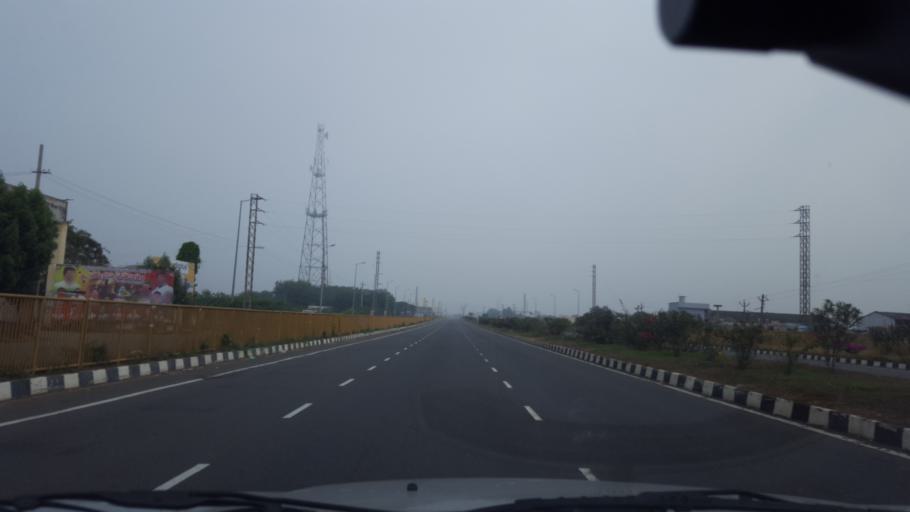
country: IN
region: Andhra Pradesh
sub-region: Prakasam
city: pedda nakkalapalem
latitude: 15.9733
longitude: 80.0972
